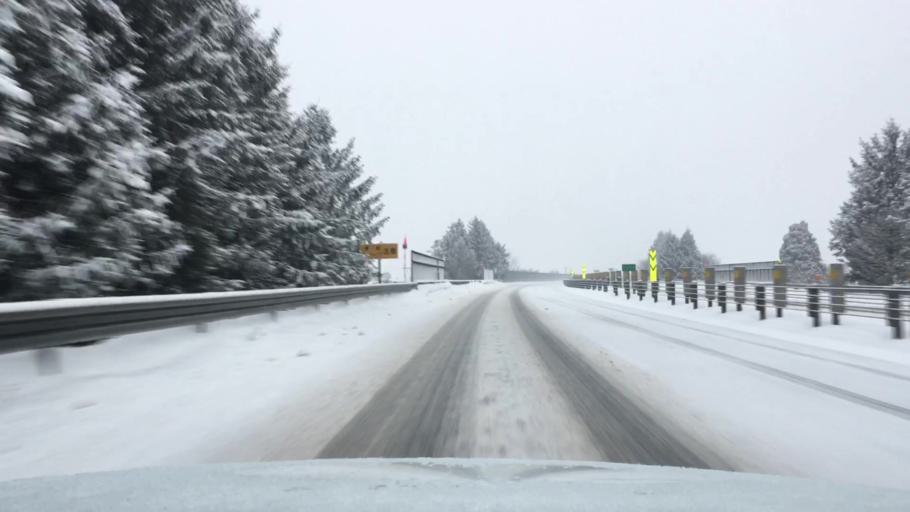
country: JP
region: Akita
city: Hanawa
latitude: 40.2717
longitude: 140.7623
